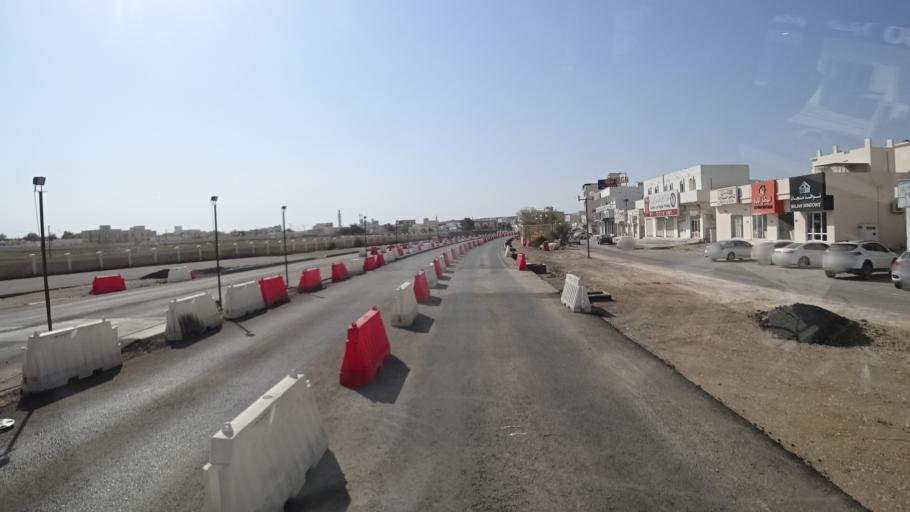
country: OM
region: Ash Sharqiyah
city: Sur
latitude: 22.5746
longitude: 59.5230
